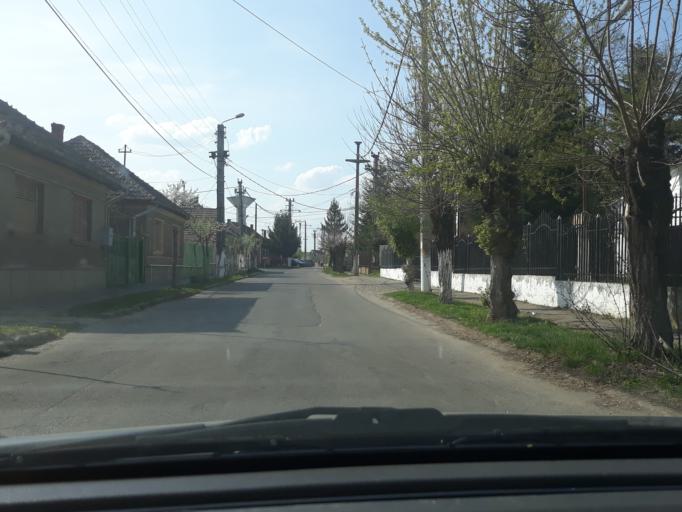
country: RO
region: Bihor
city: Margita
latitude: 47.3529
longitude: 22.3454
